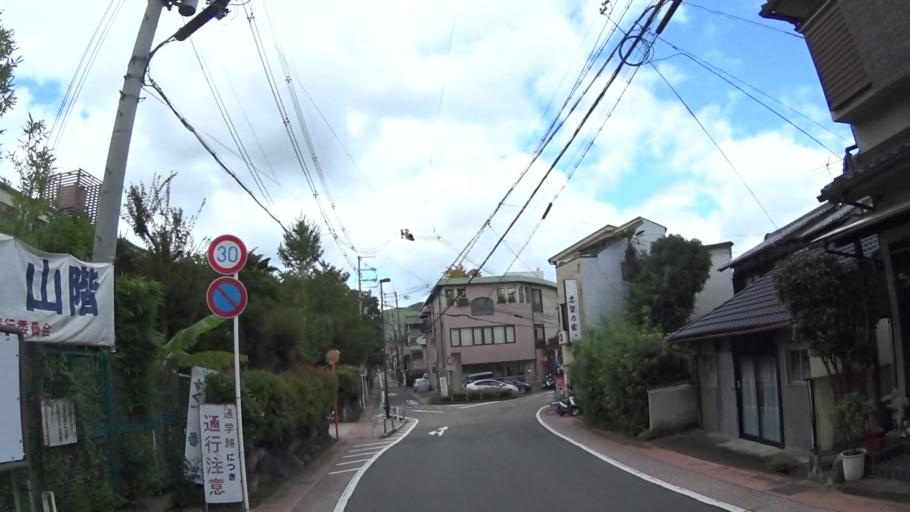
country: JP
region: Shiga Prefecture
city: Otsu-shi
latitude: 34.9831
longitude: 135.8138
